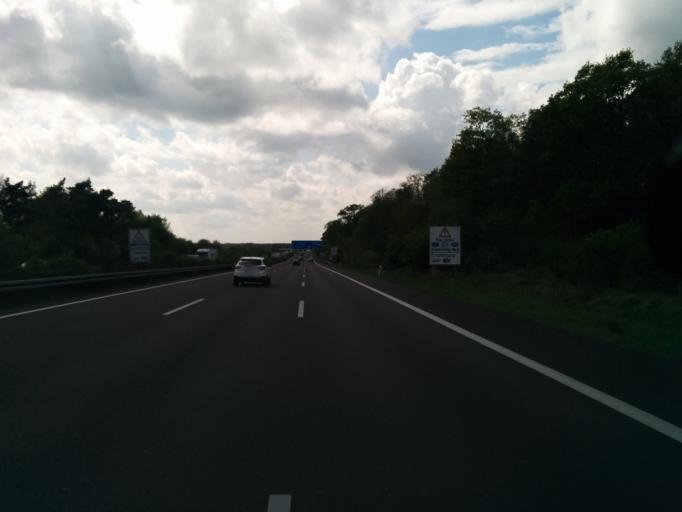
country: DE
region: Lower Saxony
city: Lehre
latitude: 52.3109
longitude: 10.7493
